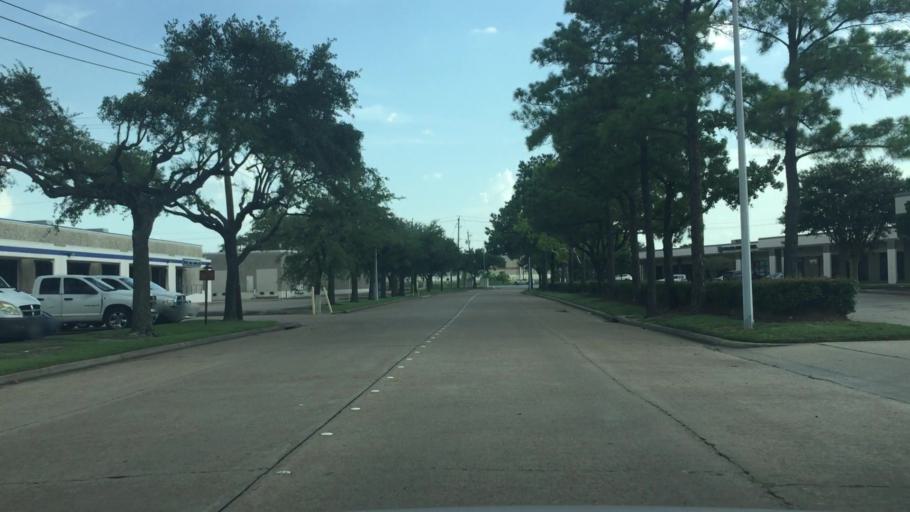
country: US
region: Texas
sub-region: Harris County
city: Spring Valley
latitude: 29.8097
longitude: -95.4685
